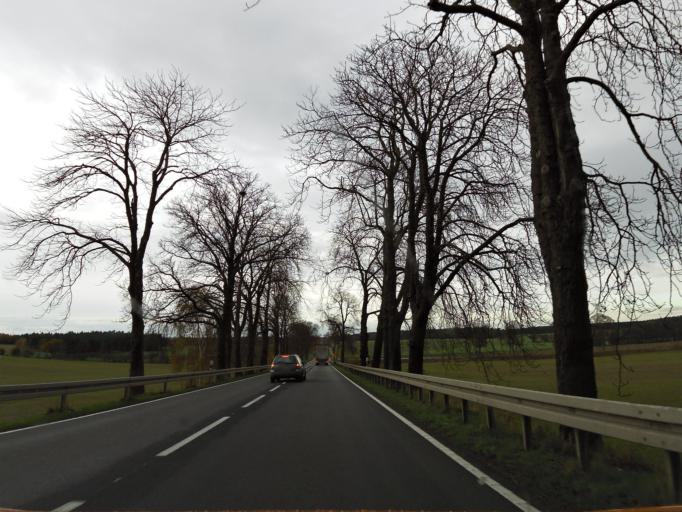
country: DE
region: Saxony-Anhalt
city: Kalbe
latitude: 52.6464
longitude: 11.2996
